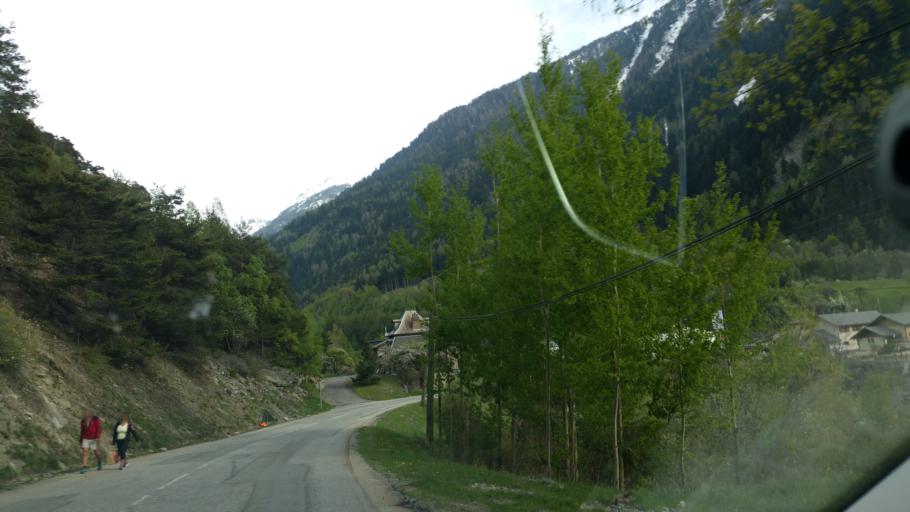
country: FR
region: Rhone-Alpes
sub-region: Departement de la Savoie
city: Modane
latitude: 45.1967
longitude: 6.6289
